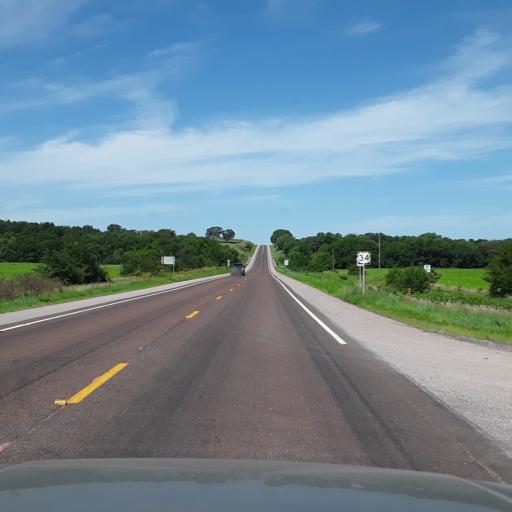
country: US
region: Nebraska
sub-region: Seward County
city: Milford
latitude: 40.8865
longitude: -96.9100
